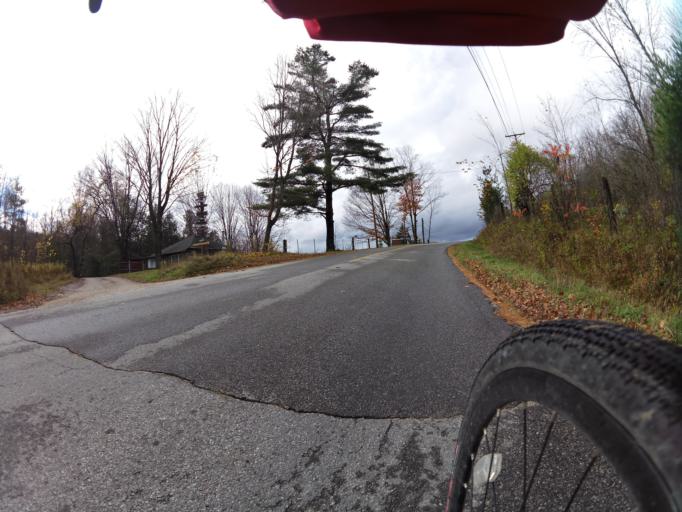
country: CA
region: Quebec
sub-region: Outaouais
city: Wakefield
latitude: 45.6915
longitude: -75.9963
